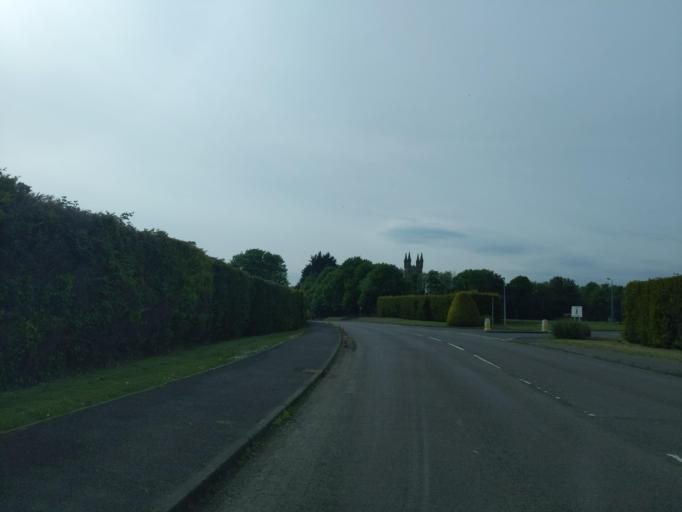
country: GB
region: England
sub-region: Devon
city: Yelverton
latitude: 50.4409
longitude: -4.0821
